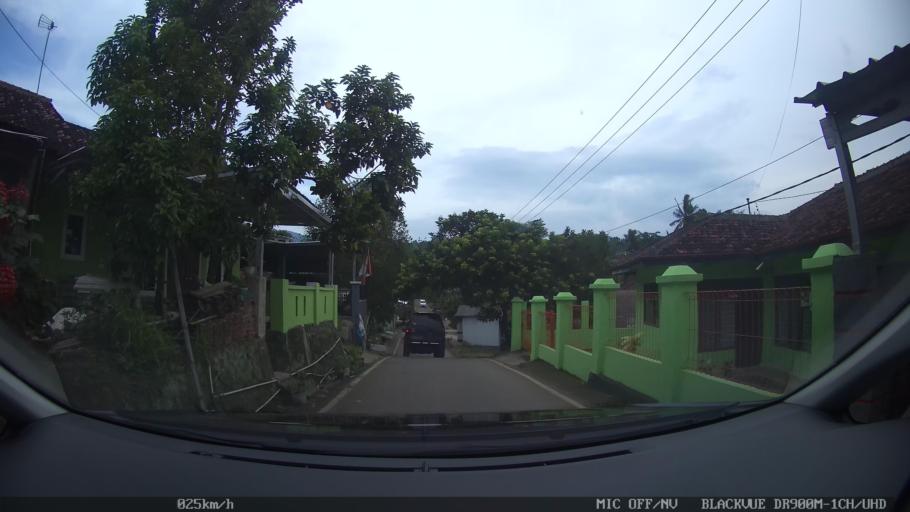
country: ID
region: Lampung
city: Kedaton
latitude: -5.3909
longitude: 105.1946
